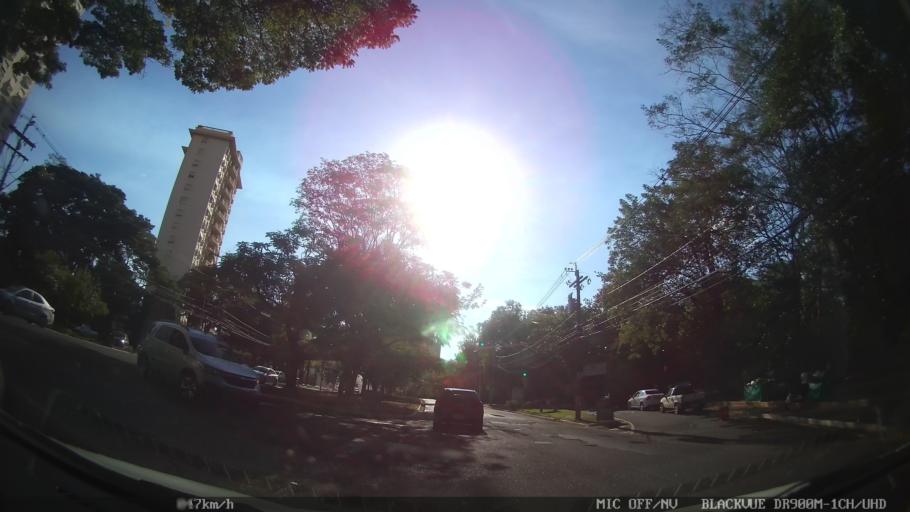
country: BR
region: Sao Paulo
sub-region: Ribeirao Preto
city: Ribeirao Preto
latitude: -21.1963
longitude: -47.7951
